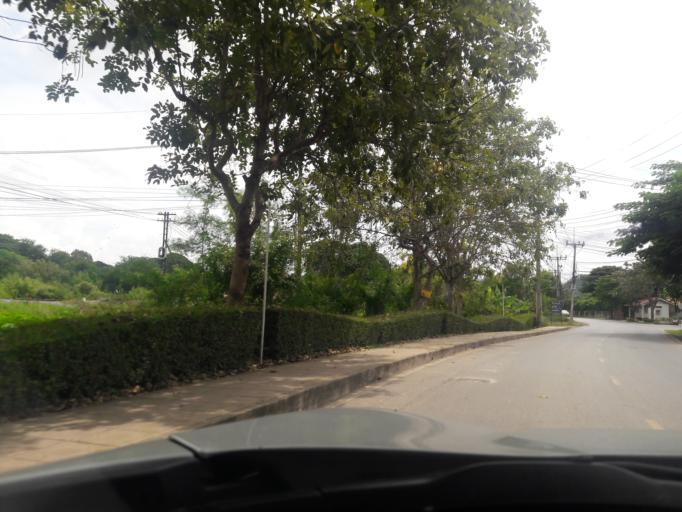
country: TH
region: Lop Buri
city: Ban Mi
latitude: 15.0414
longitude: 100.5385
